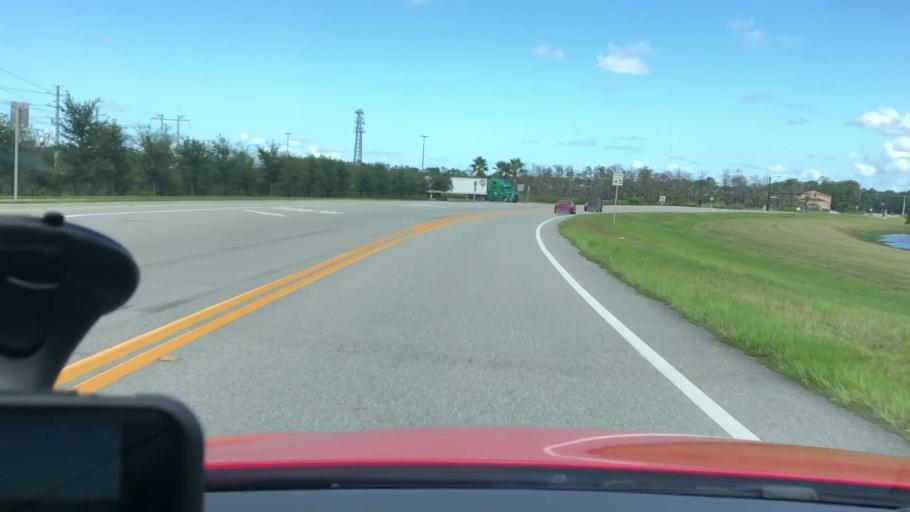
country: US
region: Florida
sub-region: Volusia County
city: Holly Hill
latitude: 29.2000
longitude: -81.0939
